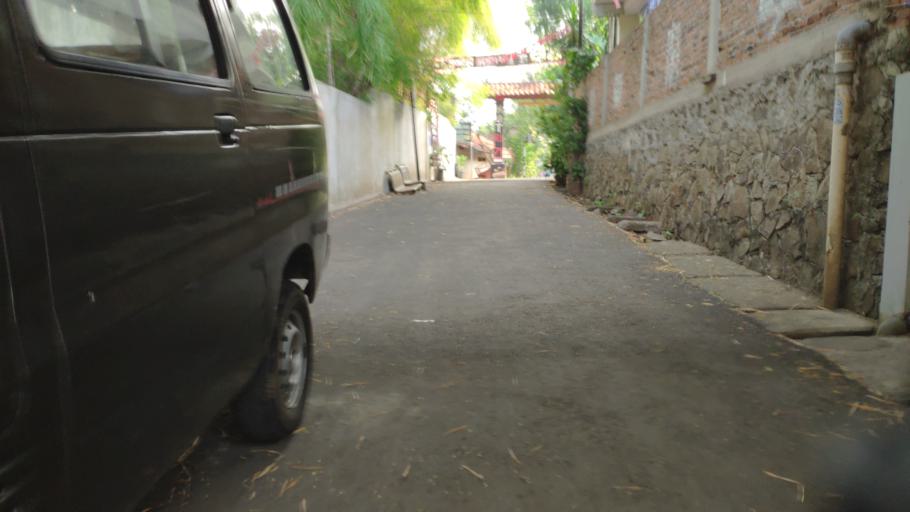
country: ID
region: West Java
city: Pamulang
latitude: -6.3025
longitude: 106.8069
